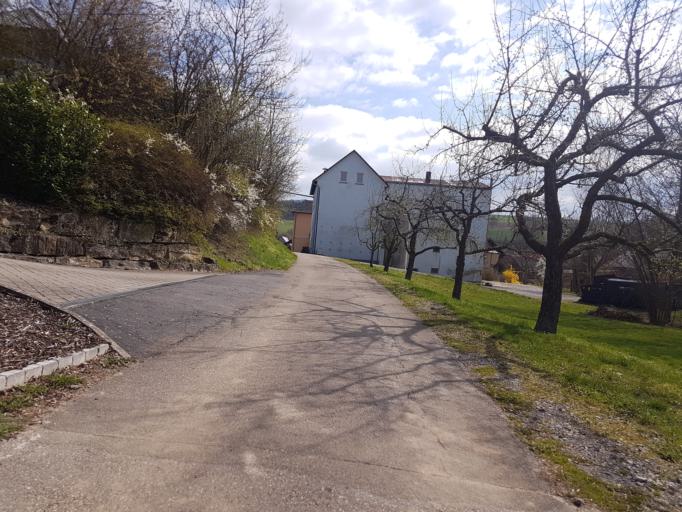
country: DE
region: Baden-Wuerttemberg
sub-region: Regierungsbezirk Stuttgart
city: Krautheim
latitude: 49.3481
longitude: 9.6104
